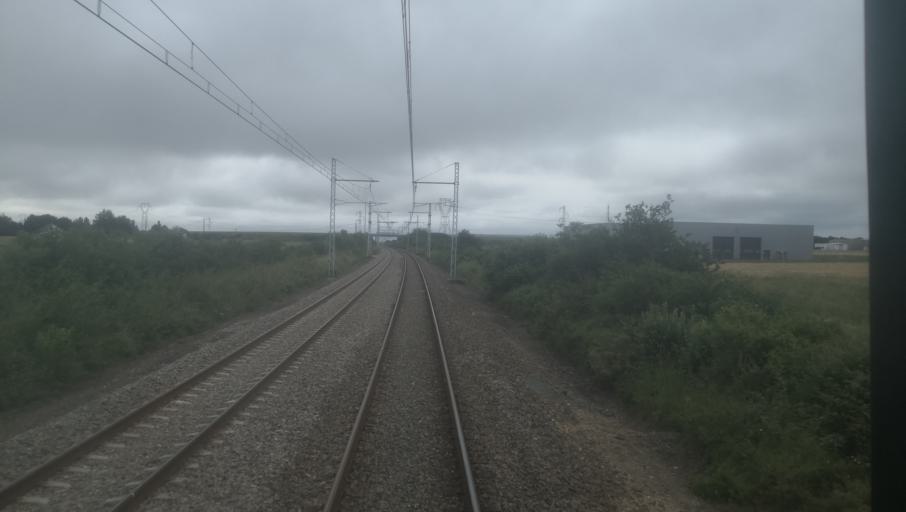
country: FR
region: Centre
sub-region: Departement de l'Indre
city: Saint-Maur
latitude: 46.7774
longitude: 1.6363
